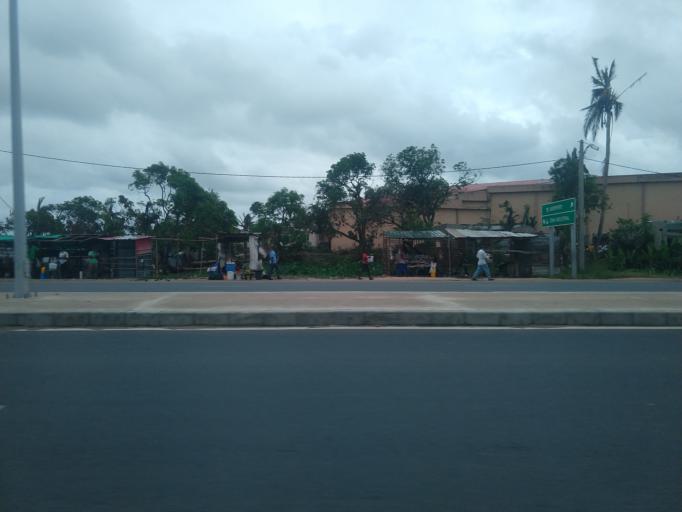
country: MZ
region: Sofala
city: Beira
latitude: -19.7849
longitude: 34.8769
